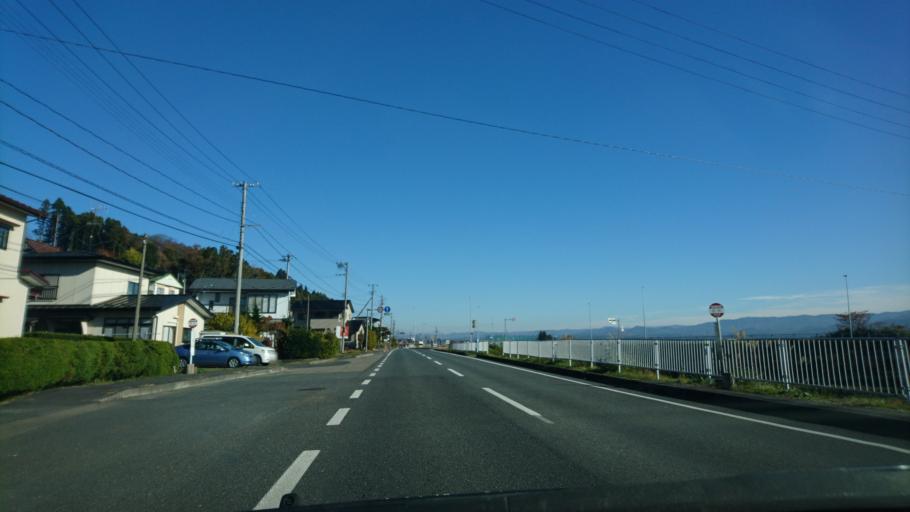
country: JP
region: Iwate
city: Mizusawa
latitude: 39.0723
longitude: 141.1302
